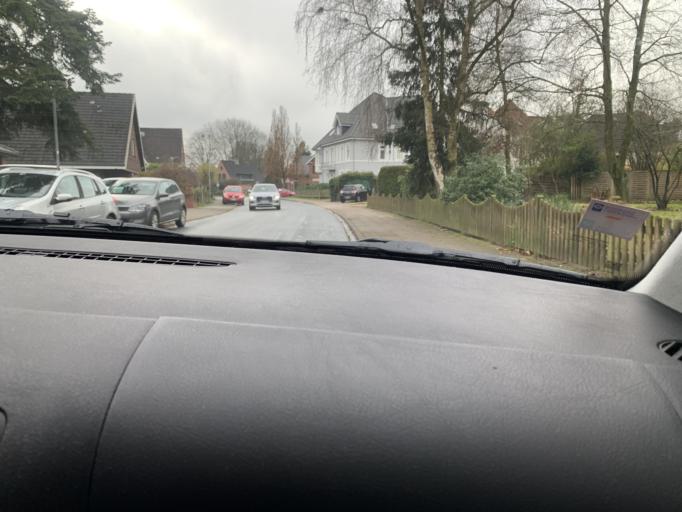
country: DE
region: Schleswig-Holstein
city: Wesseln
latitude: 54.1993
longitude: 9.0857
